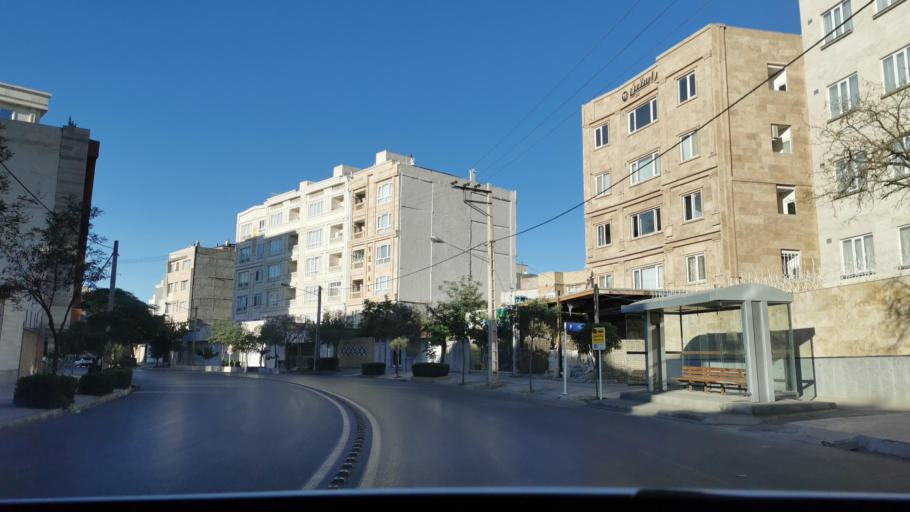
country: IR
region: Razavi Khorasan
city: Mashhad
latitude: 36.3580
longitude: 59.4975
